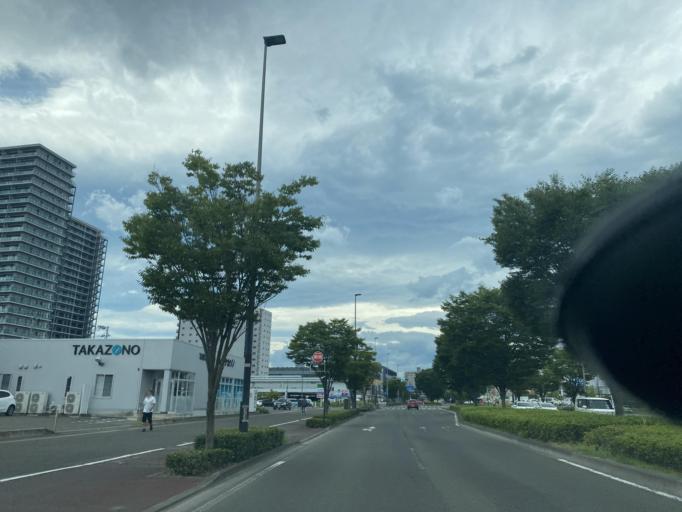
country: JP
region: Miyagi
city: Sendai
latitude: 38.2258
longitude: 140.8907
